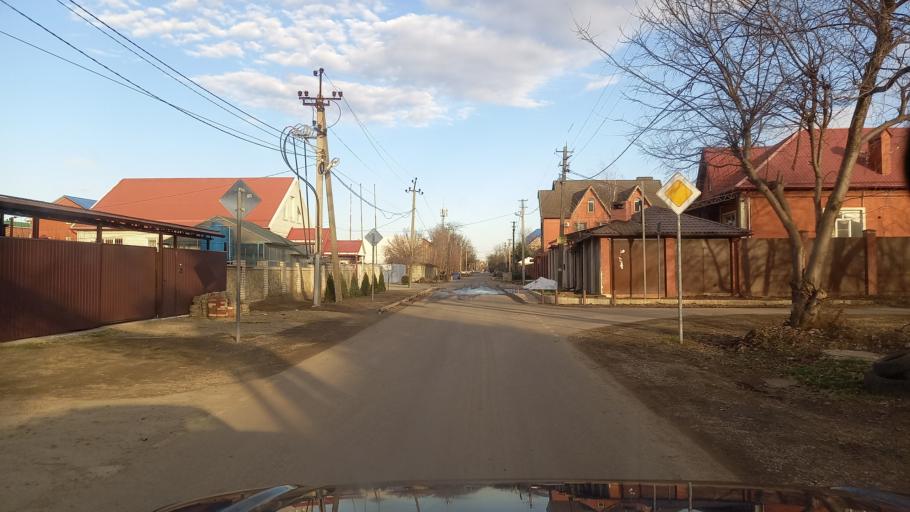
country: RU
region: Krasnodarskiy
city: Pashkovskiy
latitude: 45.0131
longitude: 39.1058
